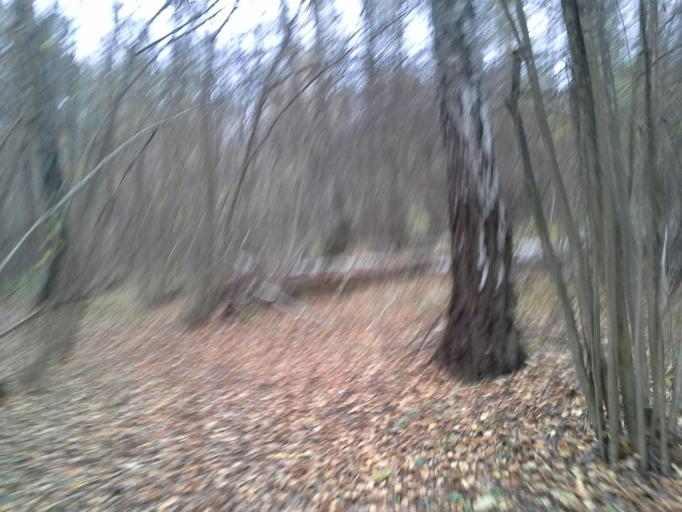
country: RU
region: Moskovskaya
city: Gorki Vtoryye
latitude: 55.6955
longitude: 37.1670
